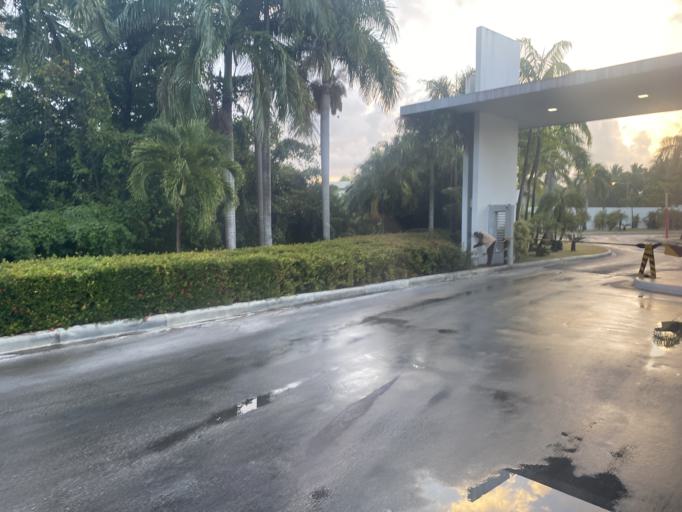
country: DO
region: San Juan
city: Punta Cana
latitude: 18.7145
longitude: -68.4583
